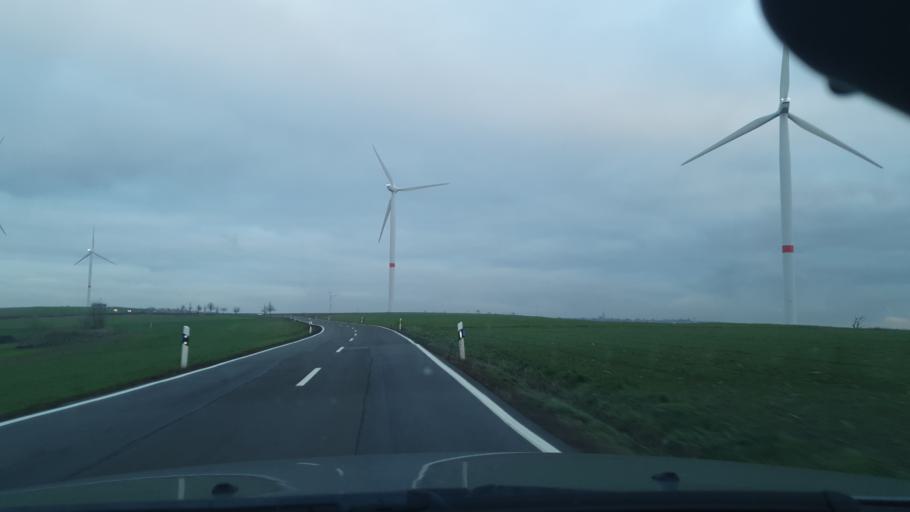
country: DE
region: Rheinland-Pfalz
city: Rosenkopf
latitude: 49.3553
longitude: 7.4438
